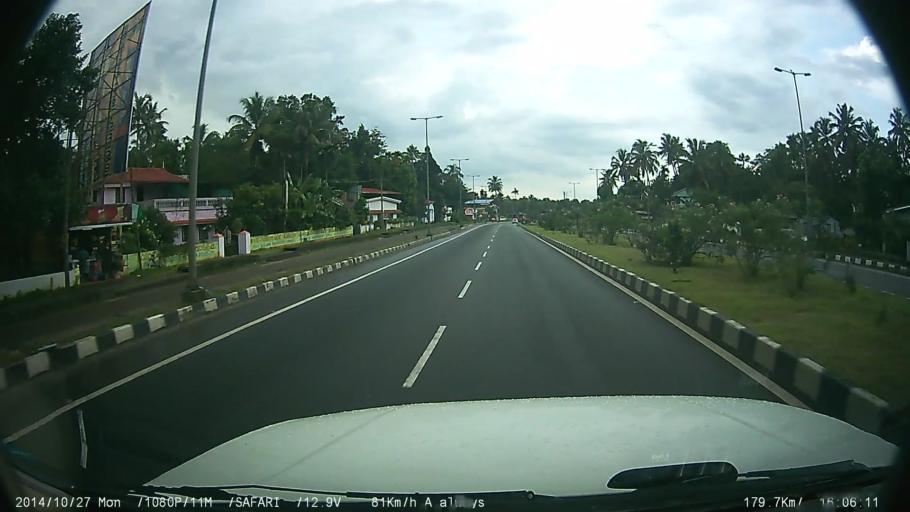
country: IN
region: Kerala
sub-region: Thrissur District
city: Kizhake Chalakudi
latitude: 10.3545
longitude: 76.3172
